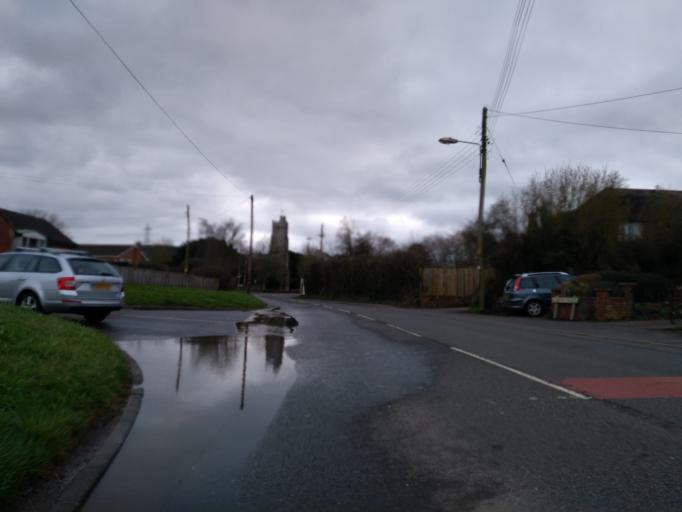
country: GB
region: England
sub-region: Devon
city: Heavitree
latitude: 50.7734
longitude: -3.5053
